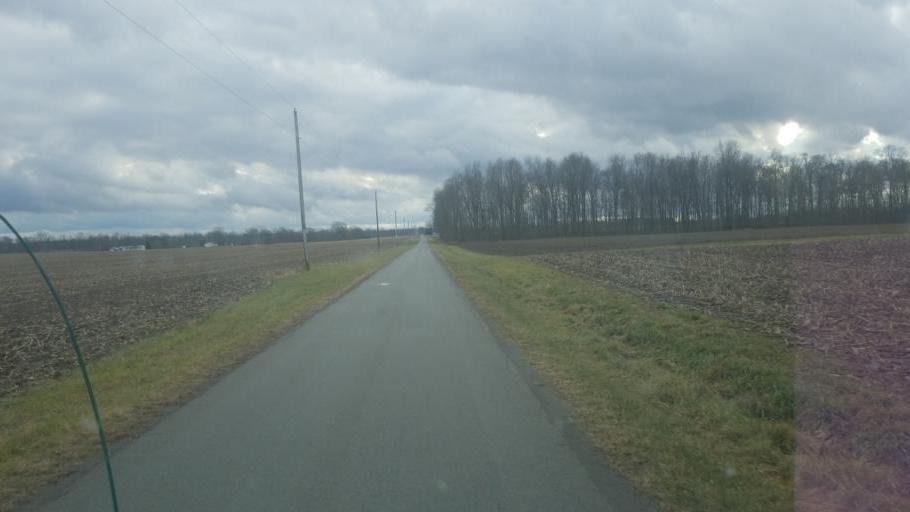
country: US
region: Ohio
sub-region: Wyandot County
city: Upper Sandusky
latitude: 40.7807
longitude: -83.1499
